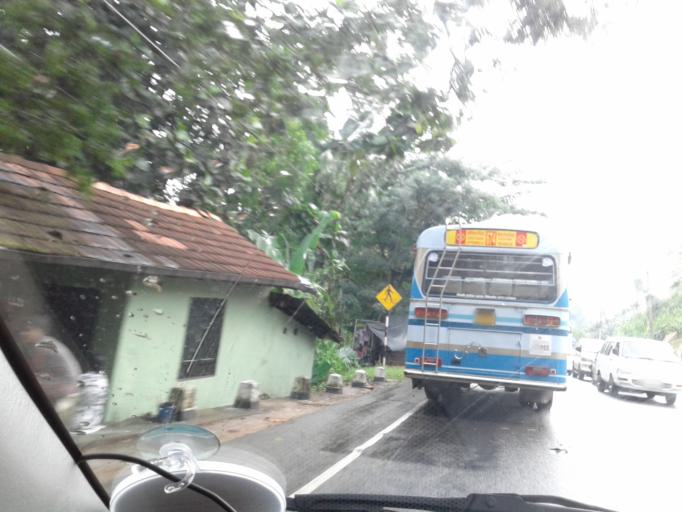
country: LK
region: Central
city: Kadugannawa
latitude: 7.2358
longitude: 80.3152
